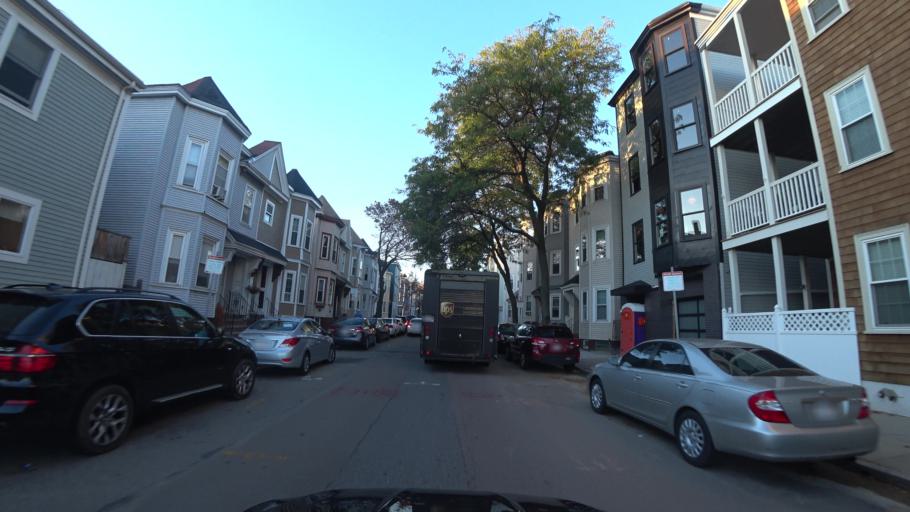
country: US
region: Massachusetts
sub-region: Suffolk County
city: South Boston
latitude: 42.3307
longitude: -71.0398
